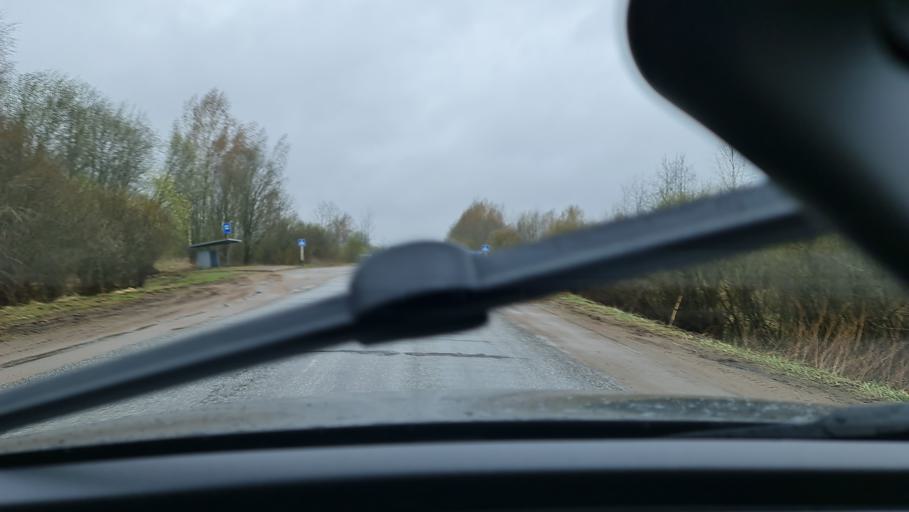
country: RU
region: Novgorod
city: Kresttsy
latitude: 58.0154
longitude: 32.7866
